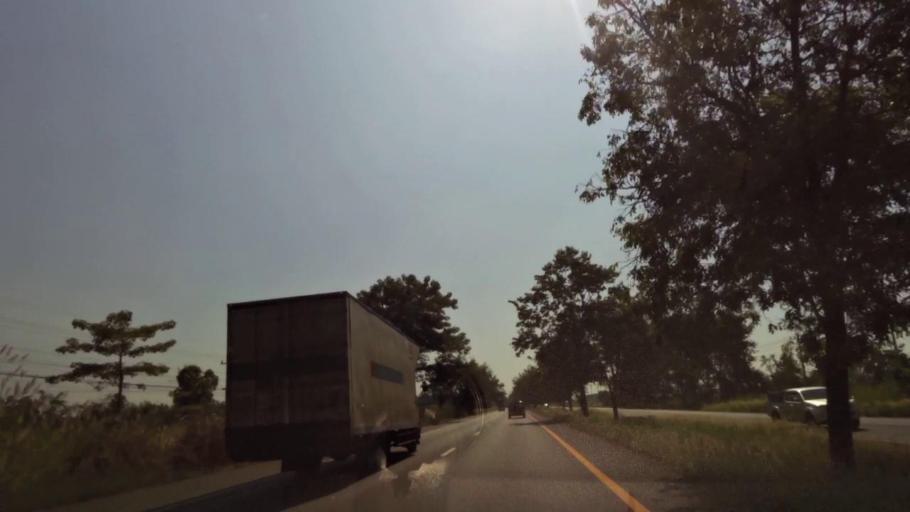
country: TH
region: Nakhon Sawan
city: Kao Liao
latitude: 15.9410
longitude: 100.1138
